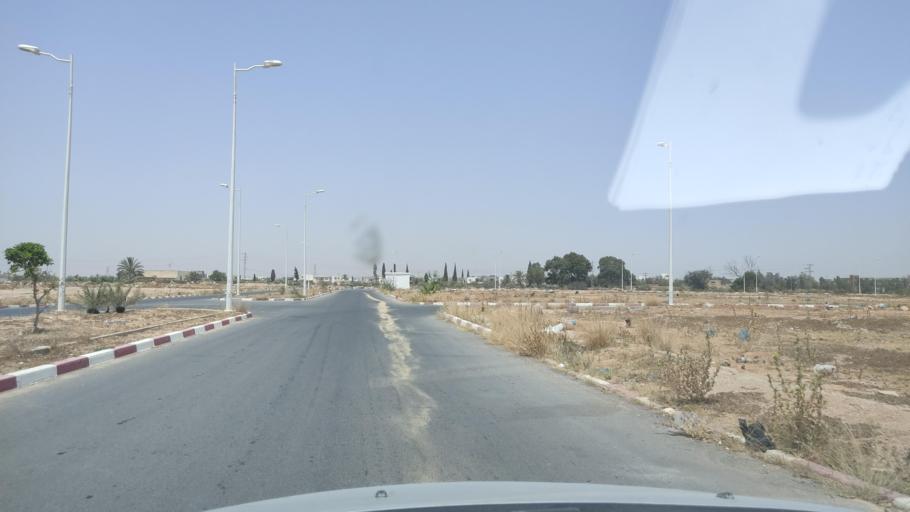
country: TN
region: Safaqis
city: Sfax
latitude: 34.7088
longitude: 10.7202
